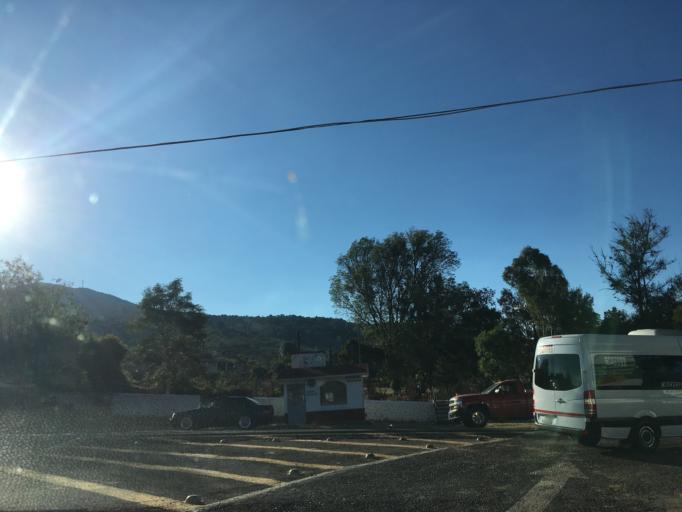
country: MX
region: Michoacan
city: Tzintzuntzan
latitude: 19.6235
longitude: -101.5768
